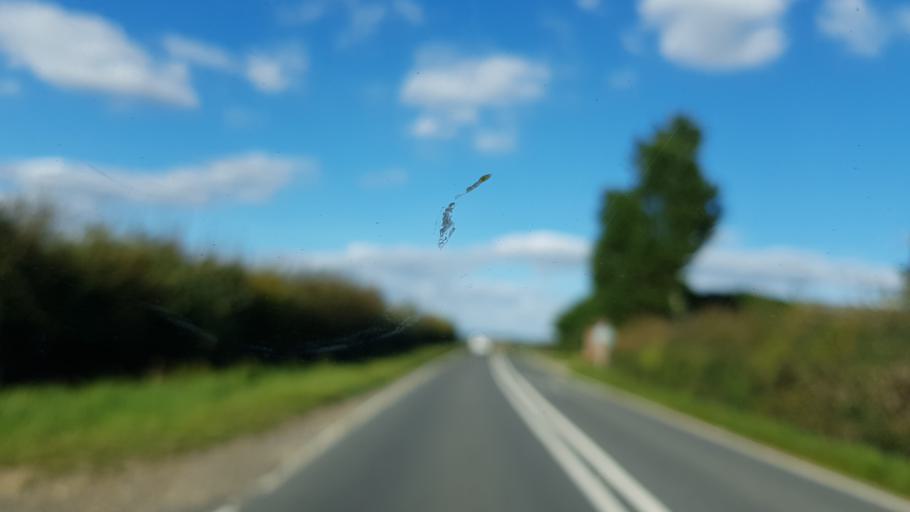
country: GB
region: England
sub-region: West Sussex
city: Petworth
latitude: 51.0400
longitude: -0.6406
